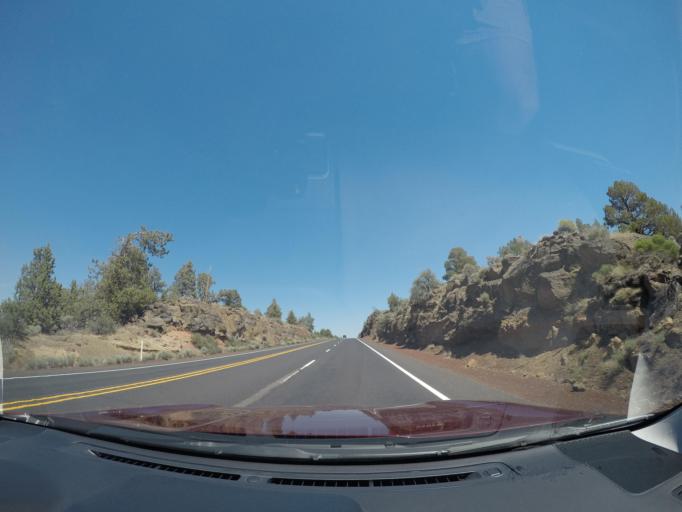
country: US
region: Oregon
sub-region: Deschutes County
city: Sisters
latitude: 44.2949
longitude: -121.3915
